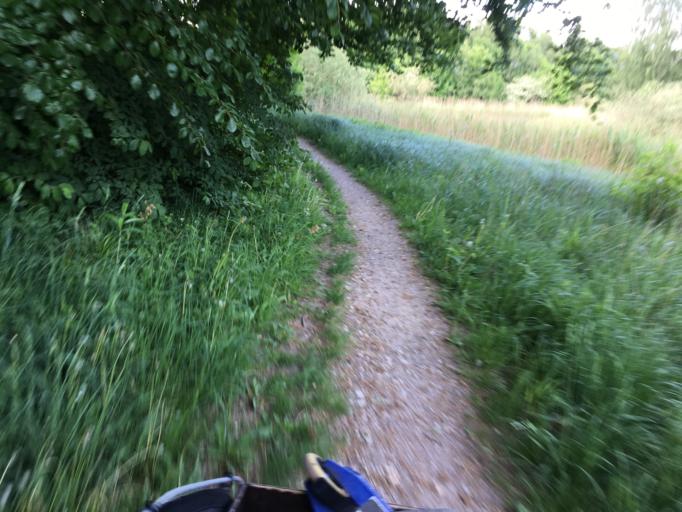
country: DK
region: Capital Region
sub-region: Ballerup Kommune
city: Ballerup
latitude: 55.7543
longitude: 12.3637
